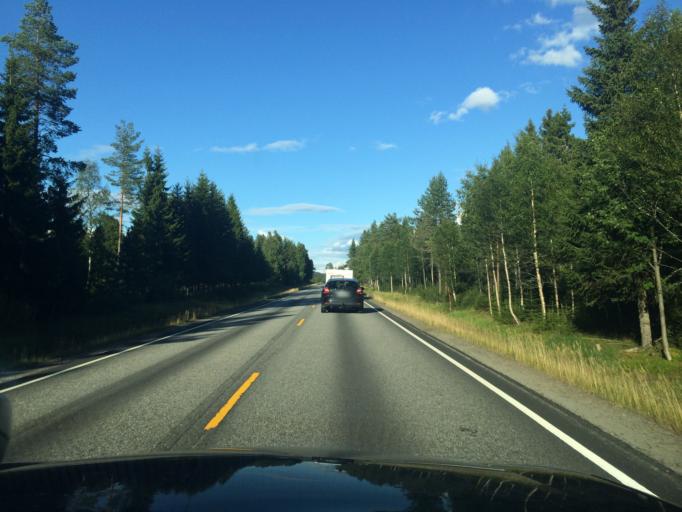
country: NO
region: Hedmark
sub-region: Elverum
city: Elverum
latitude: 61.0176
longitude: 11.8505
